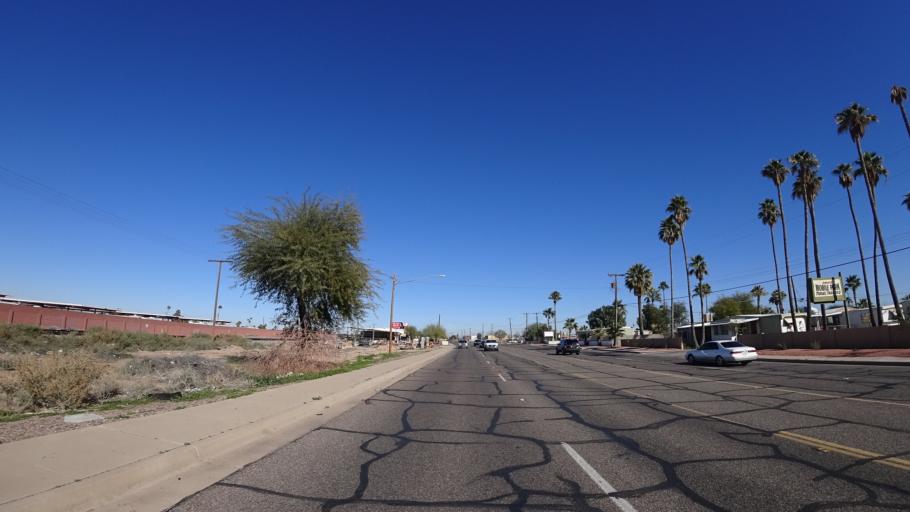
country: US
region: Arizona
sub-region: Maricopa County
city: Goodyear
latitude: 33.4266
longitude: -112.3546
